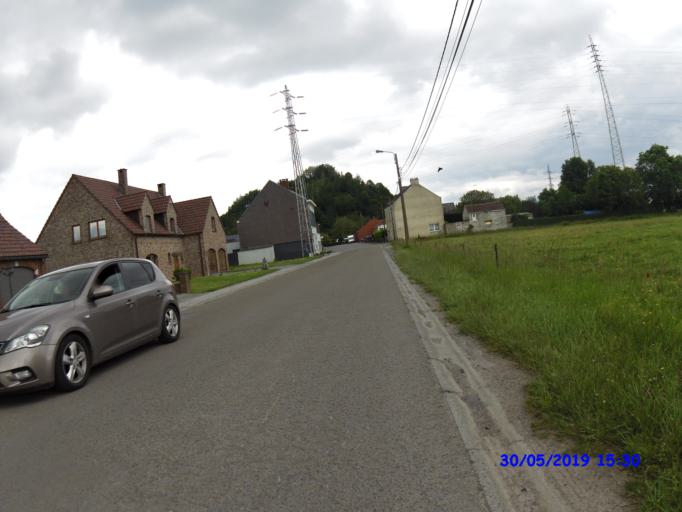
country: BE
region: Wallonia
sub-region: Province du Hainaut
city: Courcelles
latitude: 50.3987
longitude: 4.3712
